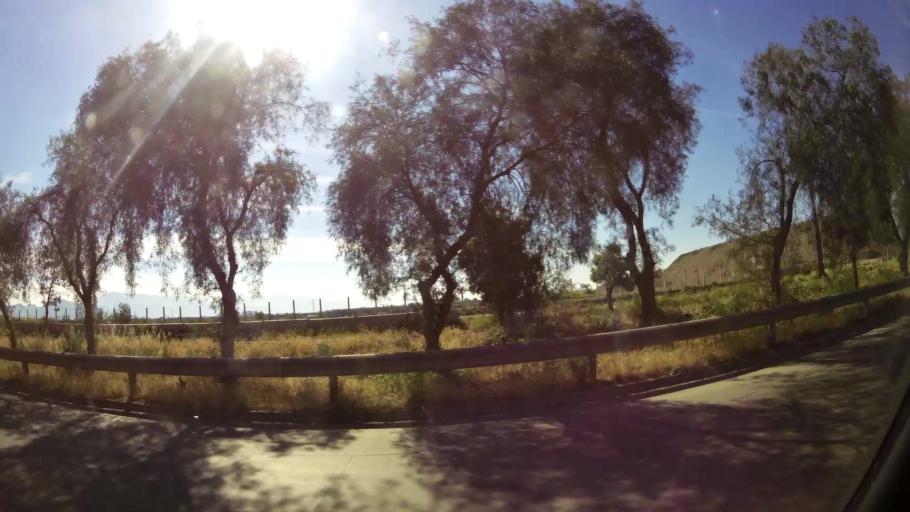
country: CL
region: Santiago Metropolitan
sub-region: Provincia de Santiago
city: Lo Prado
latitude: -33.4854
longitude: -70.7115
